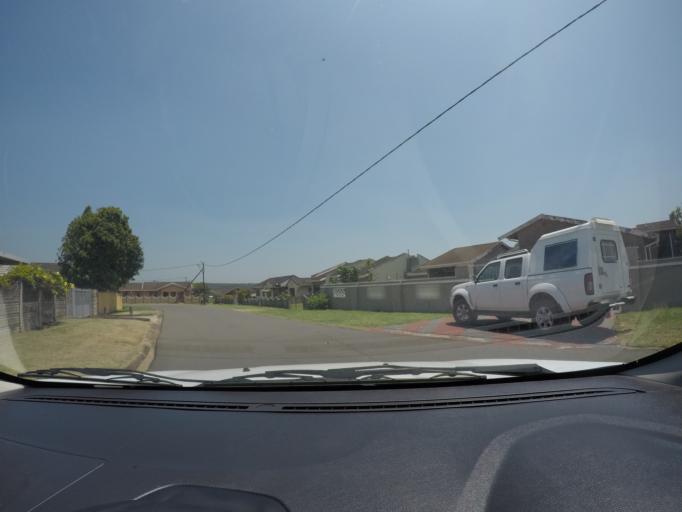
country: ZA
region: KwaZulu-Natal
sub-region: uThungulu District Municipality
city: eSikhawini
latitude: -28.8703
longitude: 31.9136
